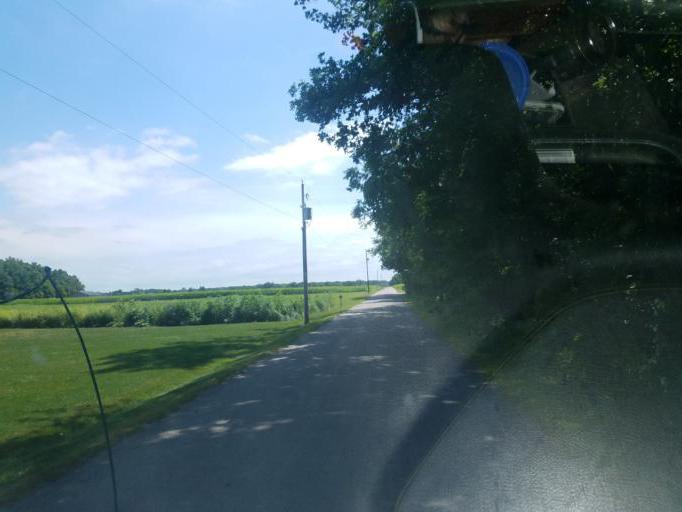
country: US
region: Indiana
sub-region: Allen County
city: Harlan
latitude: 41.1782
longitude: -84.8695
